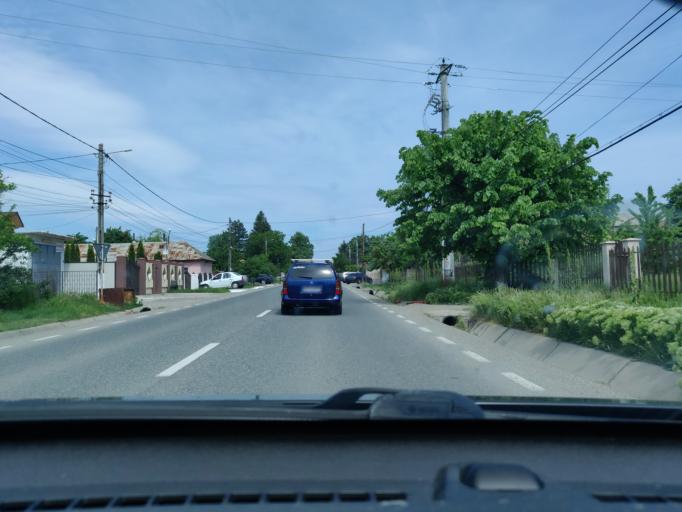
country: RO
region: Vrancea
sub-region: Comuna Bolotesti
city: Gagesti
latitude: 45.8569
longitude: 27.0527
